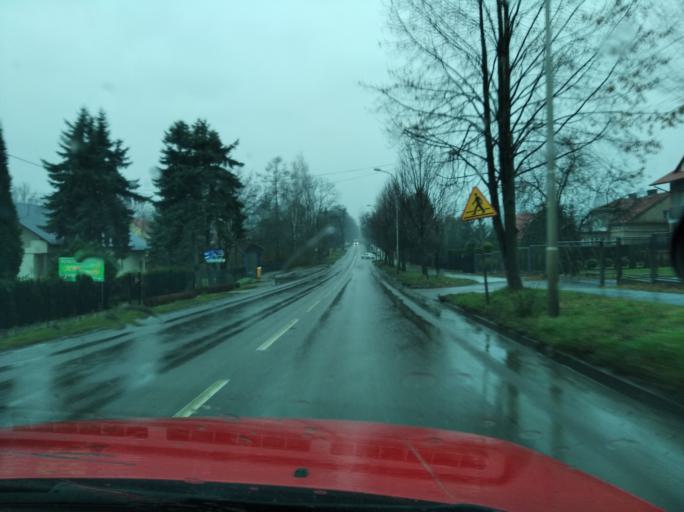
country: PL
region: Subcarpathian Voivodeship
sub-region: Powiat lancucki
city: Lancut
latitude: 50.0730
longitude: 22.2478
